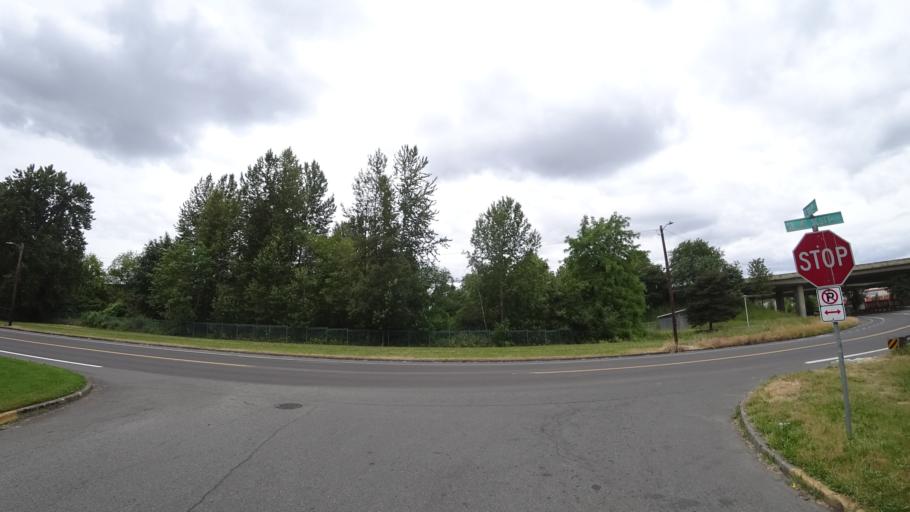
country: US
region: Oregon
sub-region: Multnomah County
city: Lents
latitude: 45.4679
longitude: -122.5644
